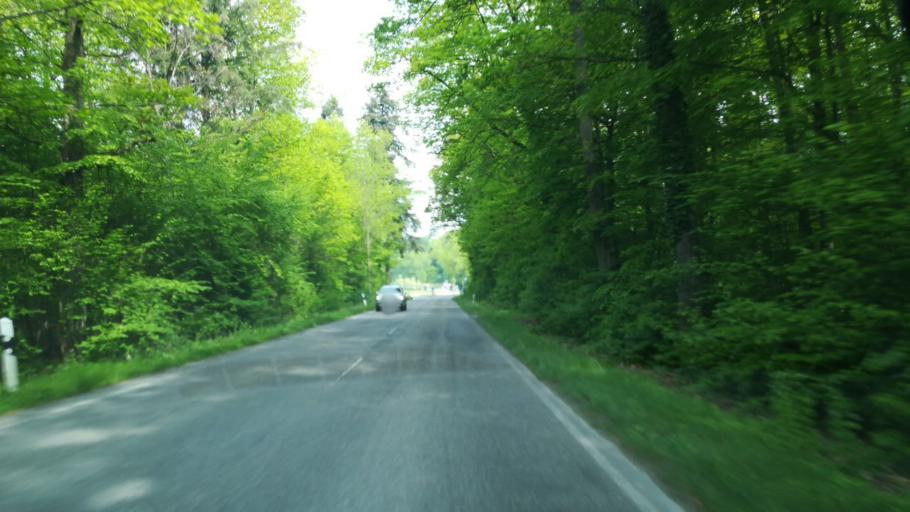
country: DE
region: Baden-Wuerttemberg
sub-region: Freiburg Region
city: Volkertshausen
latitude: 47.7734
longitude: 8.8908
